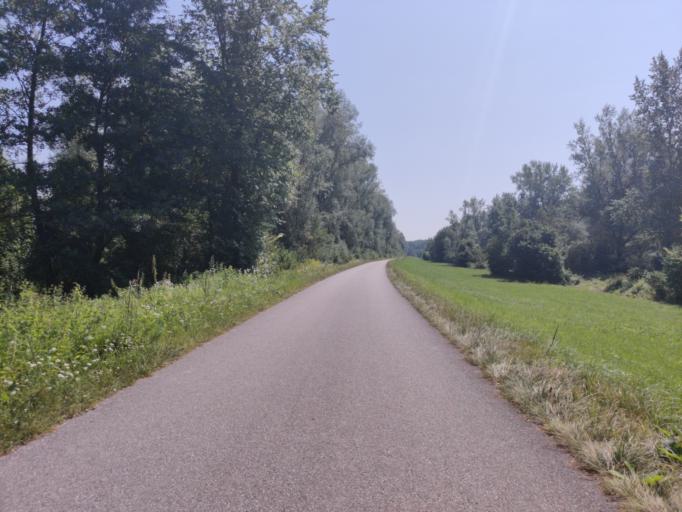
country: AT
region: Upper Austria
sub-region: Politischer Bezirk Urfahr-Umgebung
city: Feldkirchen an der Donau
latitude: 48.3229
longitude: 14.0547
